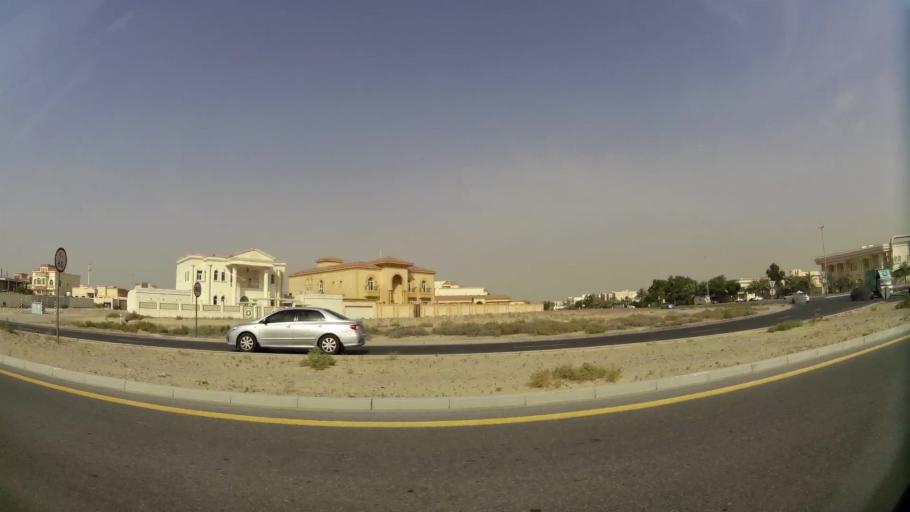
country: AE
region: Ash Shariqah
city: Sharjah
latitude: 25.2581
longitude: 55.4560
